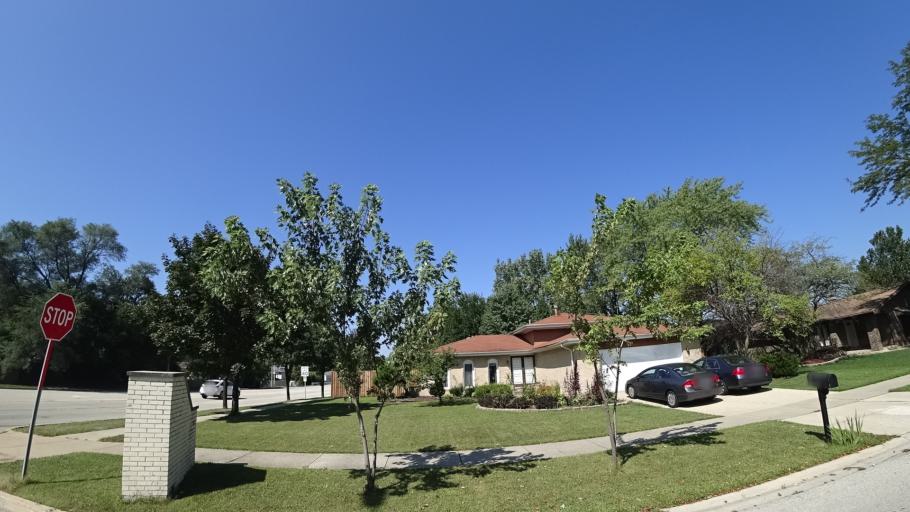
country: US
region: Illinois
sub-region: Cook County
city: Orland Park
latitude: 41.6312
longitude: -87.8264
